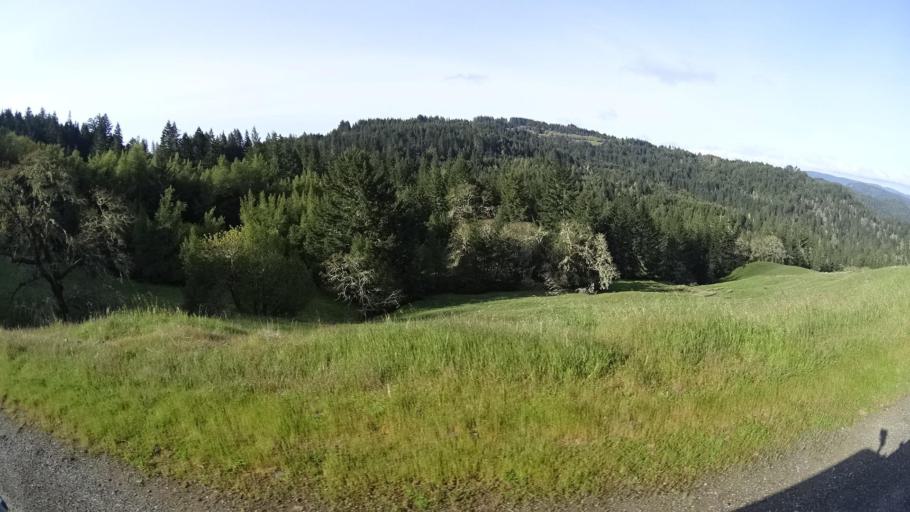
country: US
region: California
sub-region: Humboldt County
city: Hydesville
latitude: 40.6557
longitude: -123.9246
